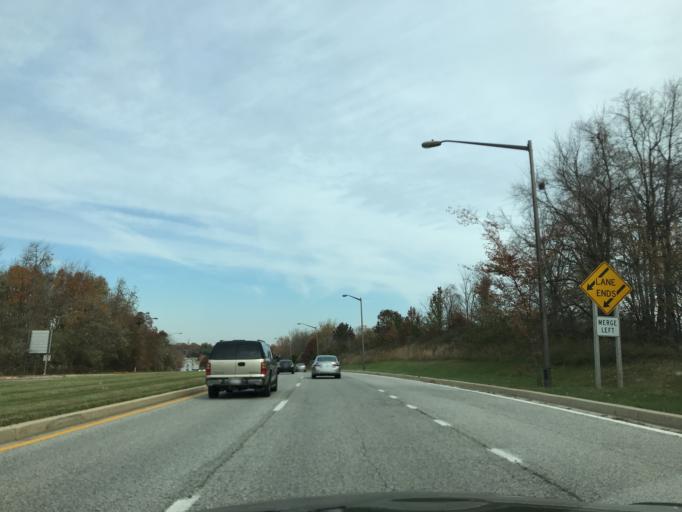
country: US
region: Maryland
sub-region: Anne Arundel County
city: Jessup
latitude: 39.1923
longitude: -76.8102
